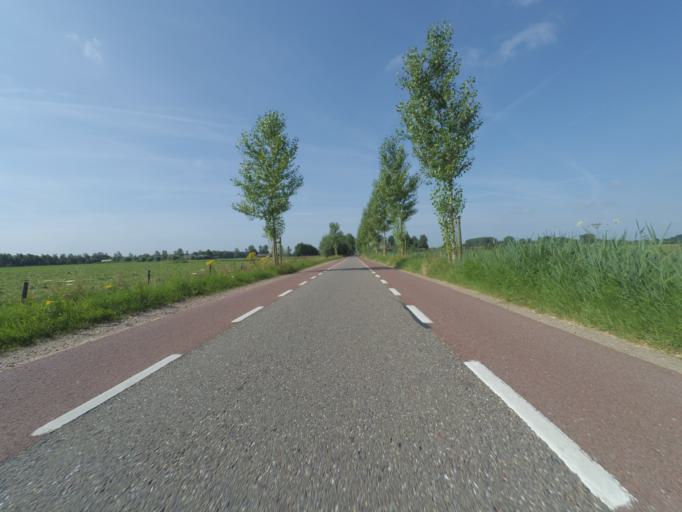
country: NL
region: Utrecht
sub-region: Gemeente Wijk bij Duurstede
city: Wijk bij Duurstede
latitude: 52.0020
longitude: 5.3621
